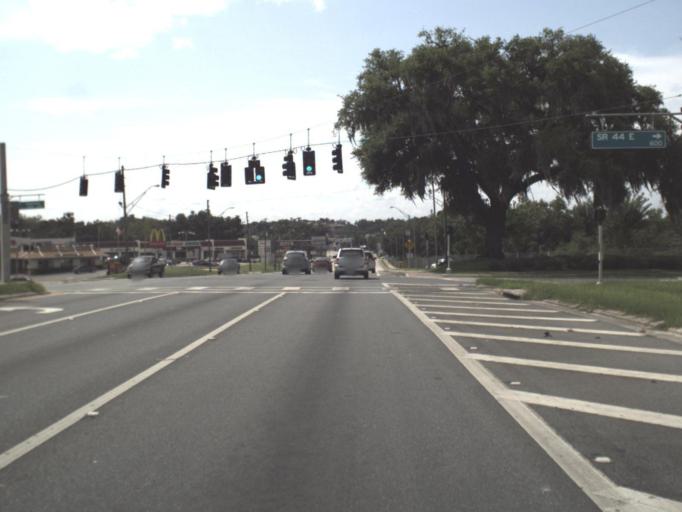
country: US
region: Florida
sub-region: Citrus County
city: Inverness
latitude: 28.8322
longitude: -82.3255
